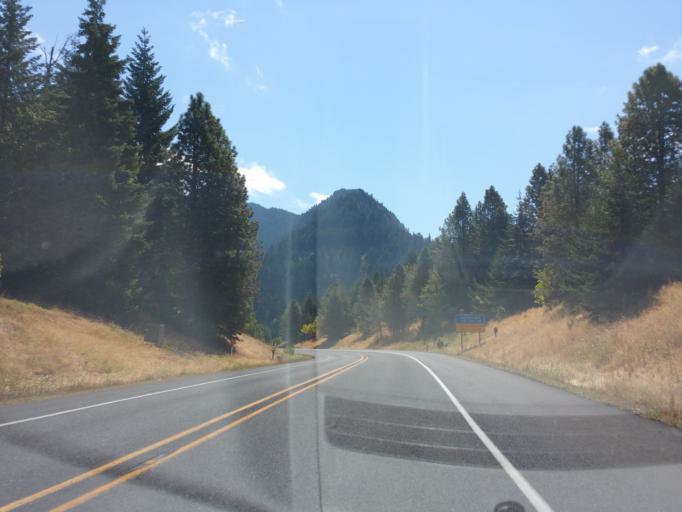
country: US
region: Oregon
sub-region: Hood River County
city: Cascade Locks
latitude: 45.6491
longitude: -121.9329
